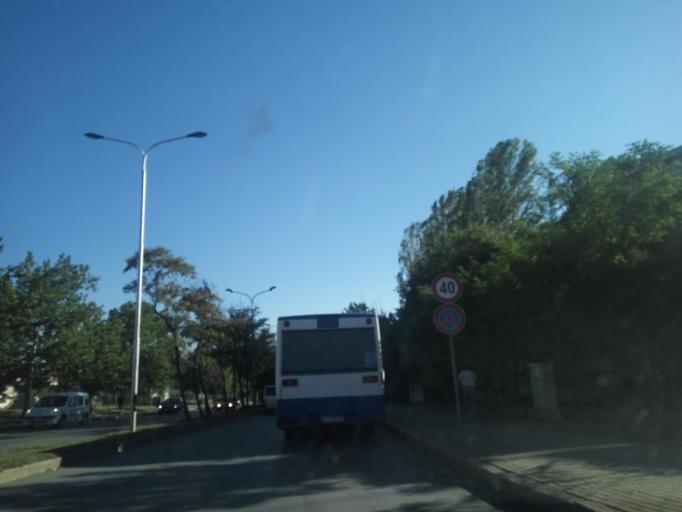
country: XK
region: Pristina
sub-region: Komuna e Prishtines
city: Pristina
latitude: 42.6501
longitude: 21.1646
